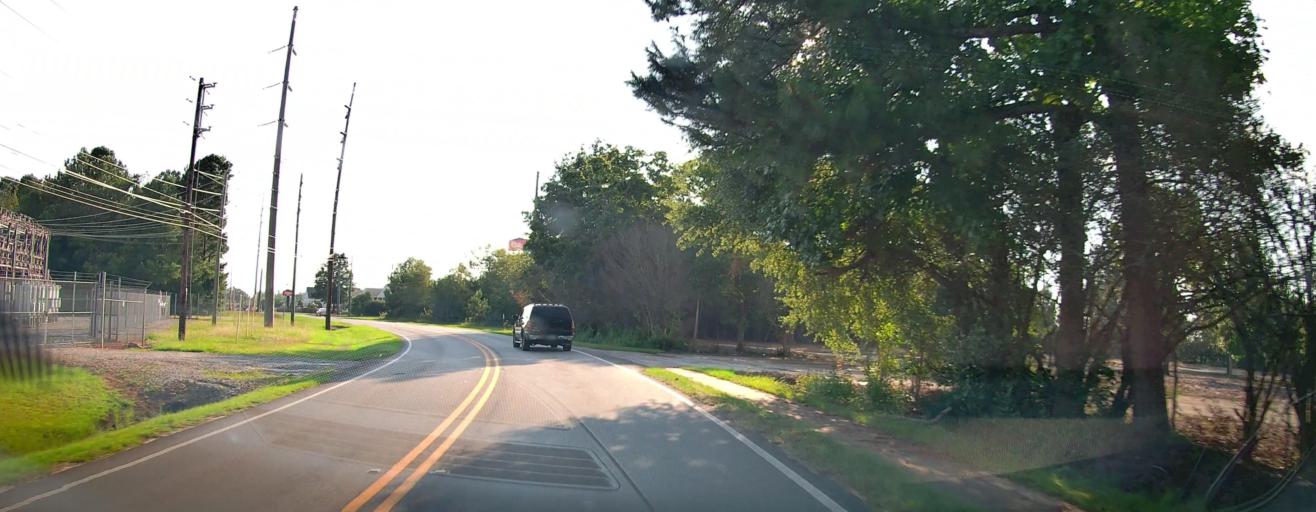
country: US
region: Georgia
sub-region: Houston County
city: Perry
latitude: 32.4699
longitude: -83.7369
